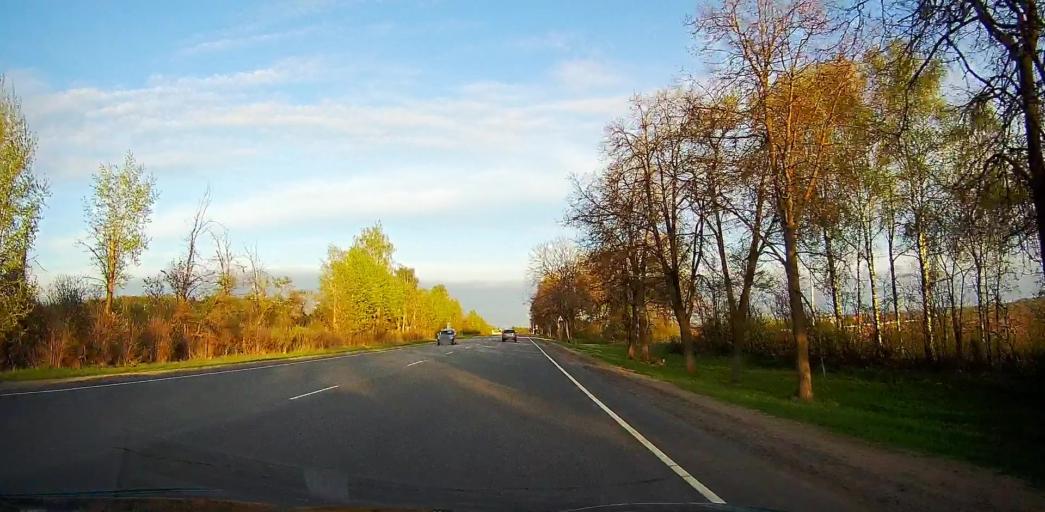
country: RU
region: Moskovskaya
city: Troitskoye
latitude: 55.2130
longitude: 38.5992
